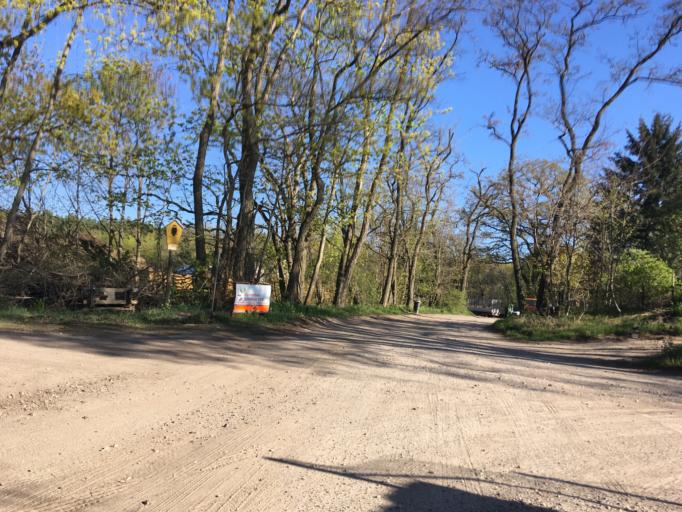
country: DE
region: Brandenburg
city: Bernau bei Berlin
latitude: 52.6935
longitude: 13.5488
